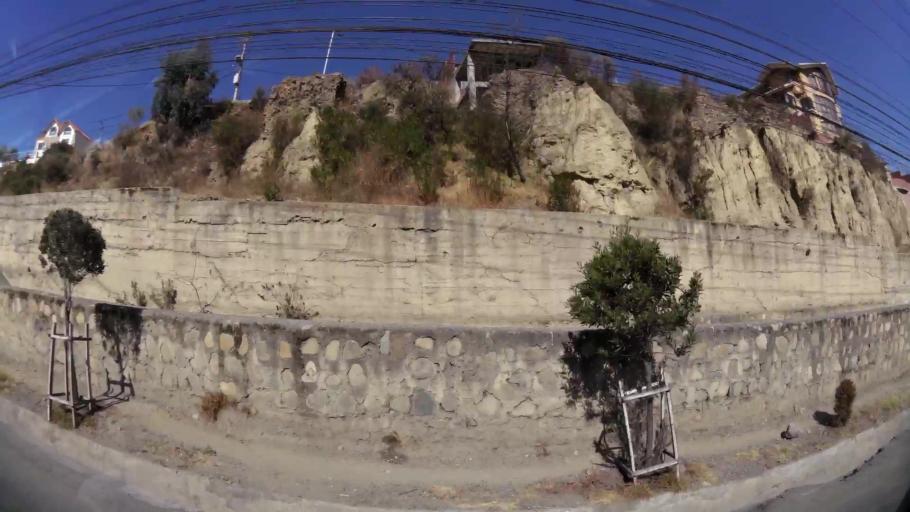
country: BO
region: La Paz
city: La Paz
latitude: -16.5206
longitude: -68.0634
